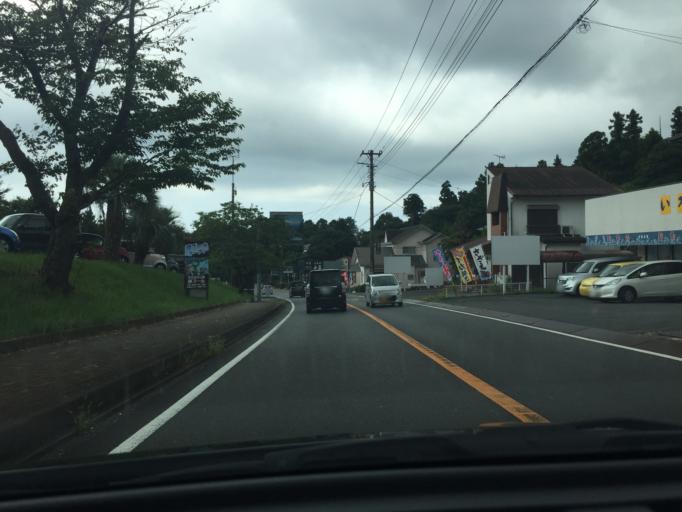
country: JP
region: Shizuoka
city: Ito
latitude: 34.9045
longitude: 139.1199
